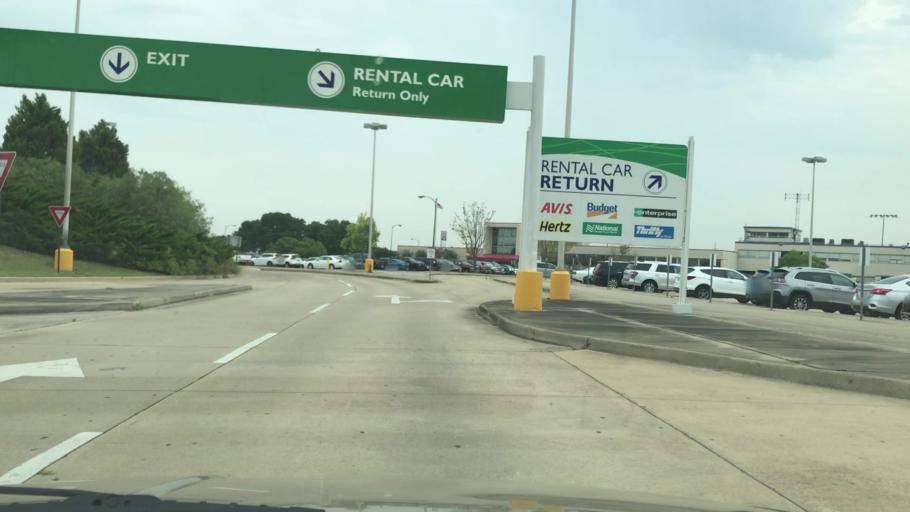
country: US
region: Louisiana
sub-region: Caddo Parish
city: Shreveport
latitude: 32.4541
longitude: -93.8278
